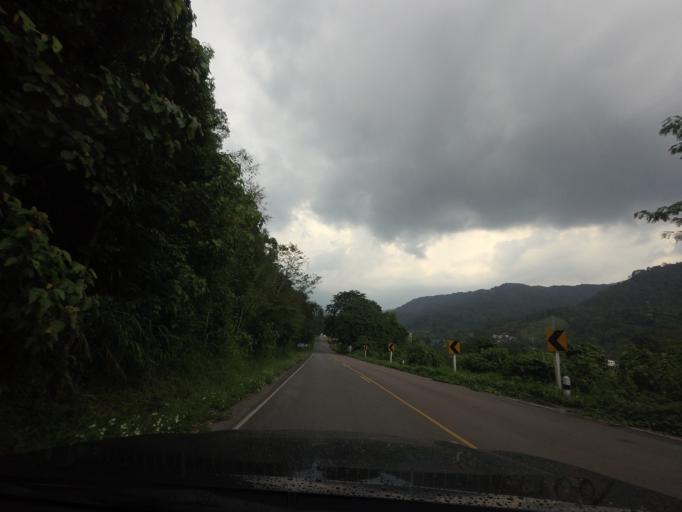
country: TH
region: Nan
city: Bo Kluea
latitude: 19.1495
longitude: 101.1514
